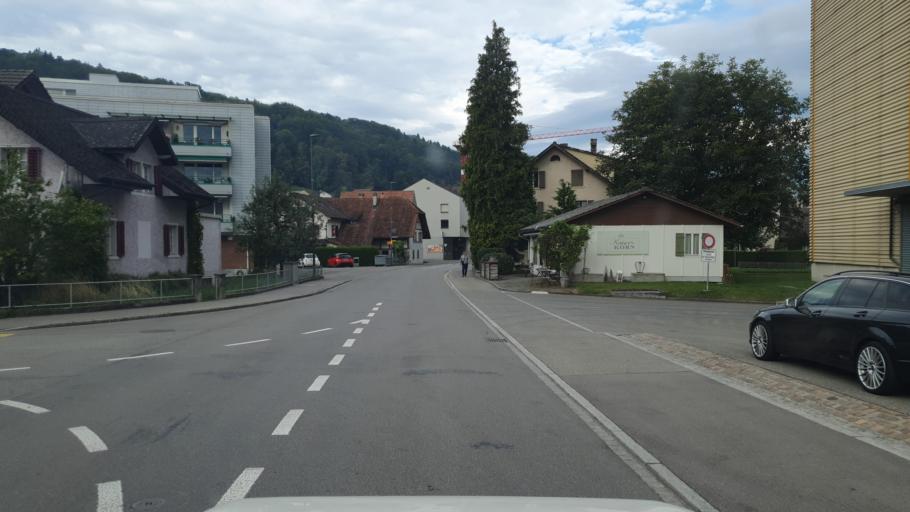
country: CH
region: Aargau
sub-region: Bezirk Bremgarten
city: Villmergen
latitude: 47.3465
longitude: 8.2472
